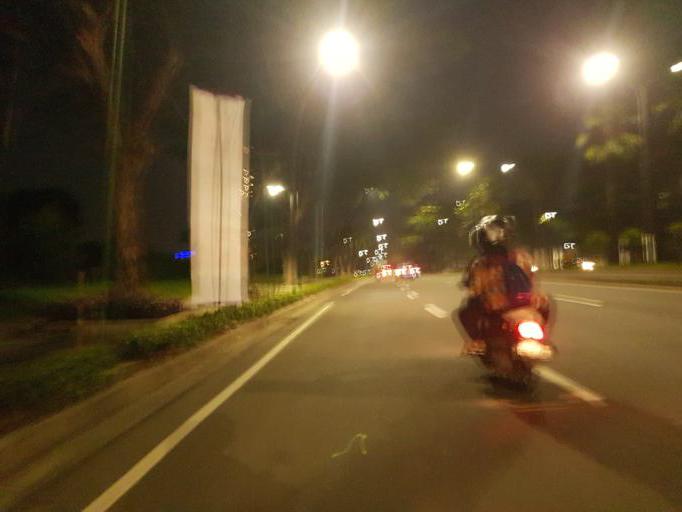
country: ID
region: West Java
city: Serpong
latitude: -6.2997
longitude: 106.6607
